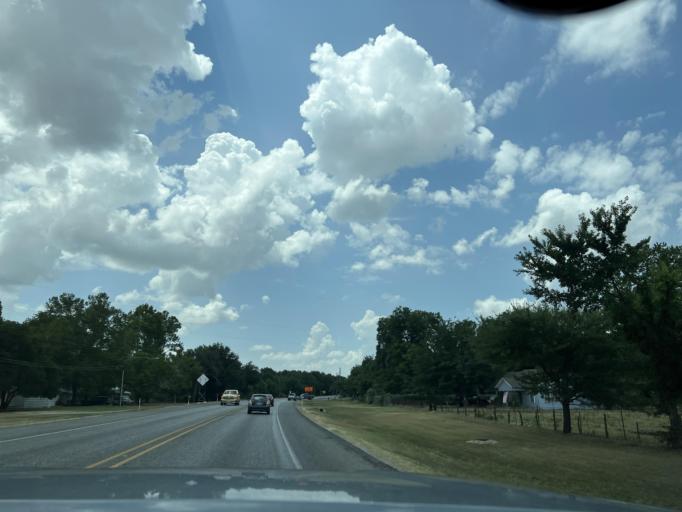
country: US
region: Texas
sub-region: Parker County
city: Springtown
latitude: 32.9589
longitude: -97.6827
